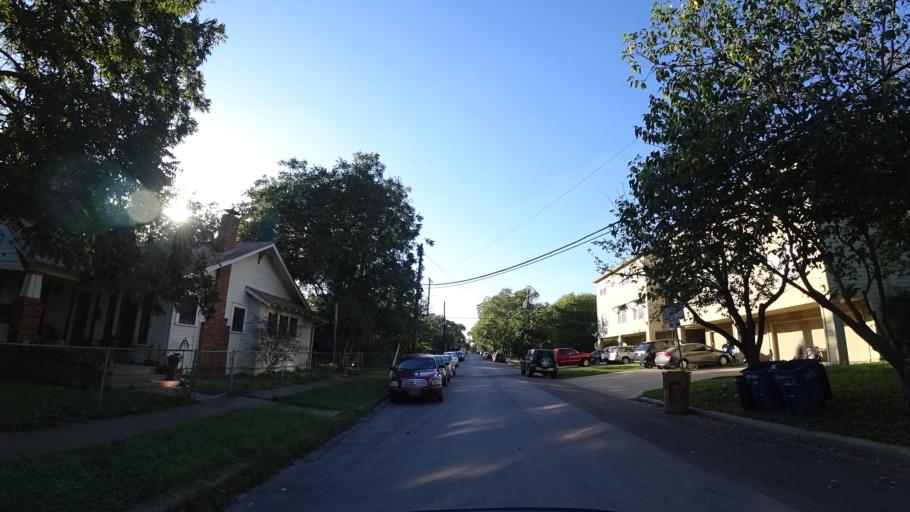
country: US
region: Texas
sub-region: Travis County
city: Austin
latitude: 30.2976
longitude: -97.7306
